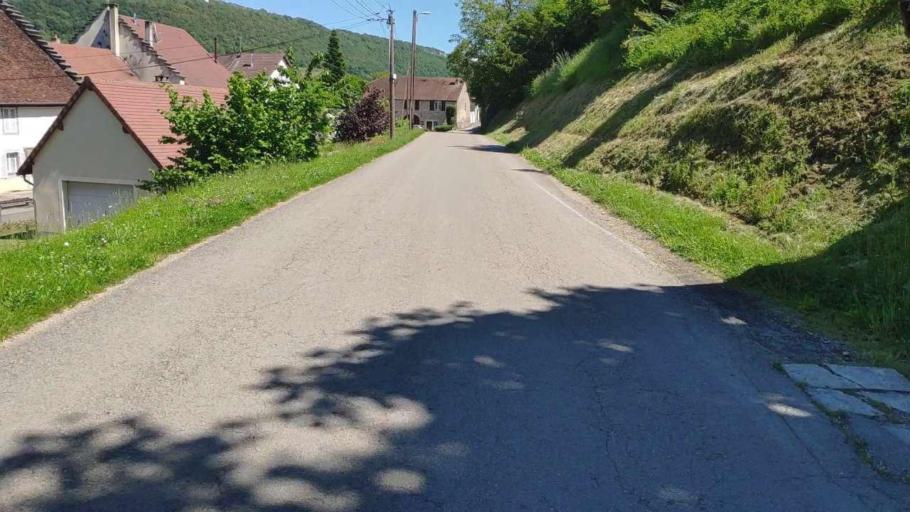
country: FR
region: Franche-Comte
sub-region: Departement du Jura
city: Perrigny
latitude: 46.7515
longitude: 5.6122
